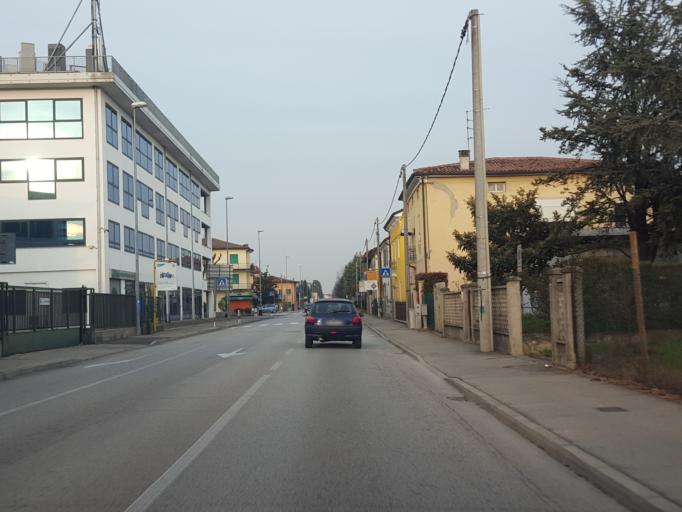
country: IT
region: Veneto
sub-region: Provincia di Vicenza
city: Vicenza
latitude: 45.5326
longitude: 11.5218
